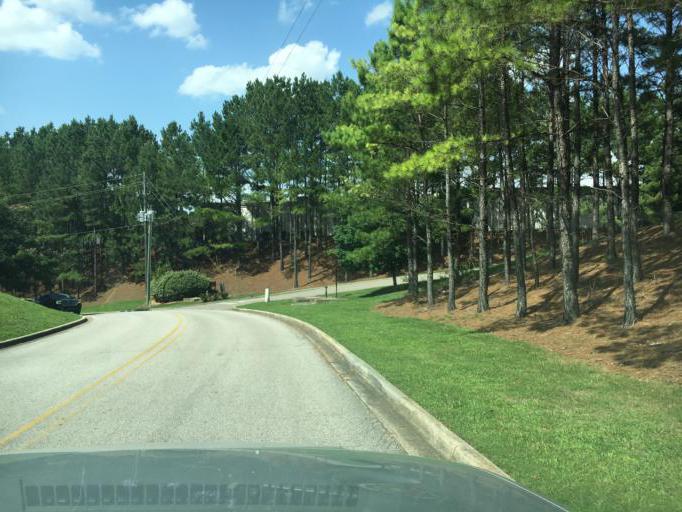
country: US
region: Alabama
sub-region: Shelby County
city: Meadowbrook
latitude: 33.4274
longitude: -86.7122
